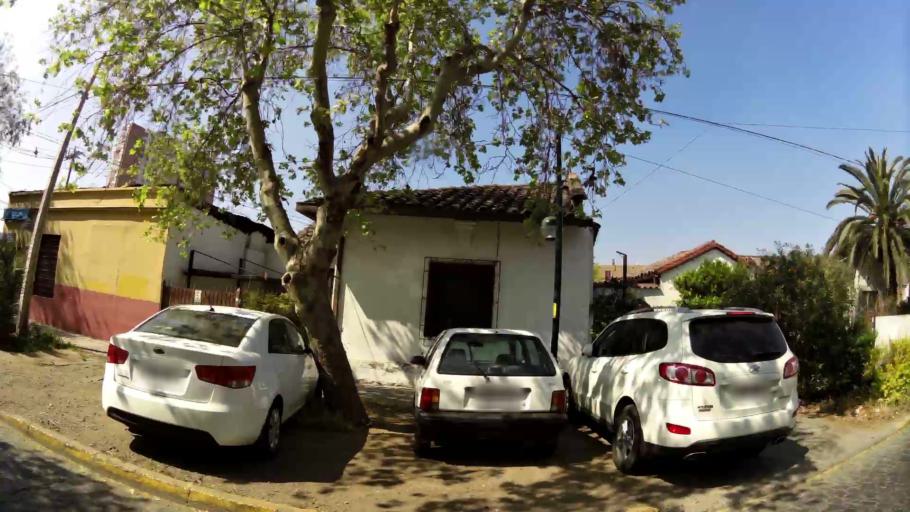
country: CL
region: Santiago Metropolitan
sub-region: Provincia de Santiago
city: Santiago
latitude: -33.4568
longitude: -70.6245
